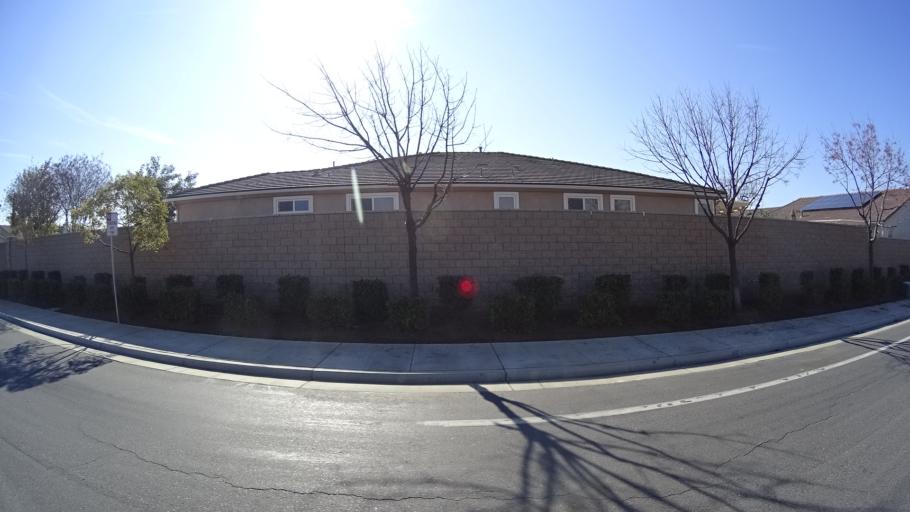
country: US
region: California
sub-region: Kern County
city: Oildale
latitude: 35.4125
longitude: -118.8889
